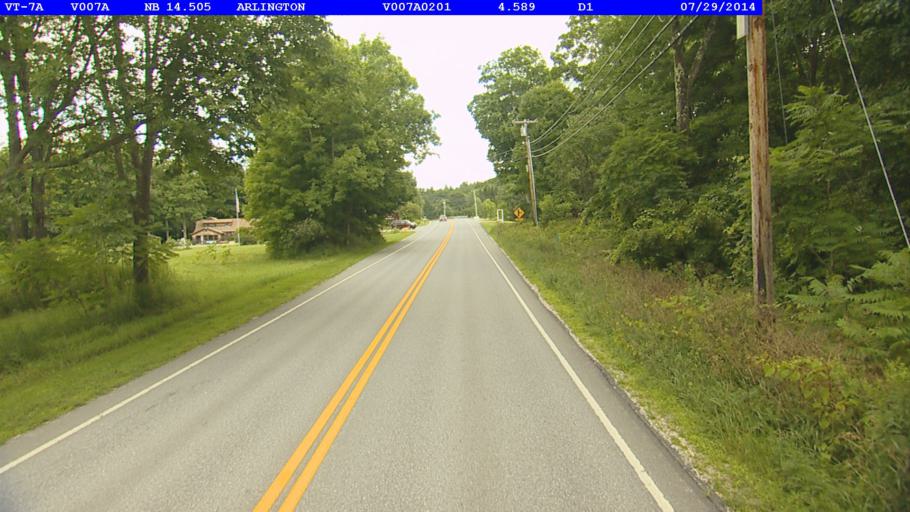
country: US
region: Vermont
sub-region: Bennington County
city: Arlington
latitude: 43.0826
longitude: -73.1464
